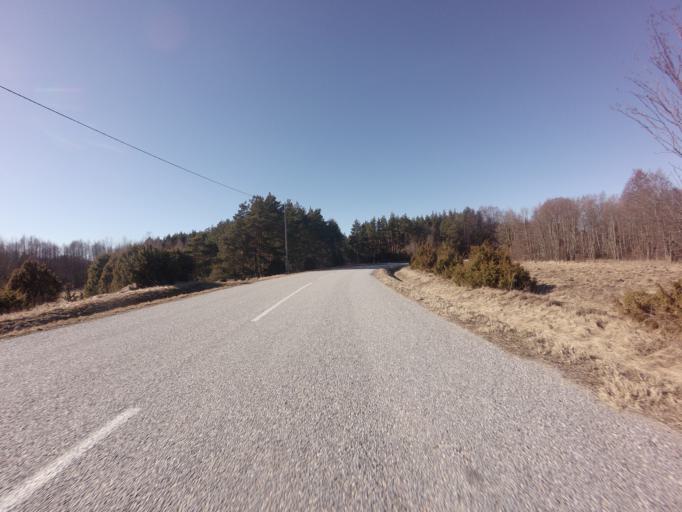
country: EE
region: Saare
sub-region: Kuressaare linn
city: Kuressaare
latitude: 58.5715
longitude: 22.4624
